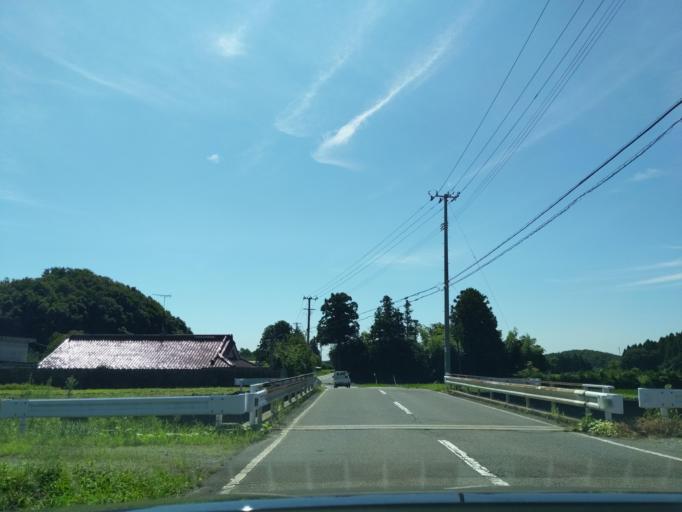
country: JP
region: Fukushima
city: Koriyama
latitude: 37.3825
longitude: 140.2616
